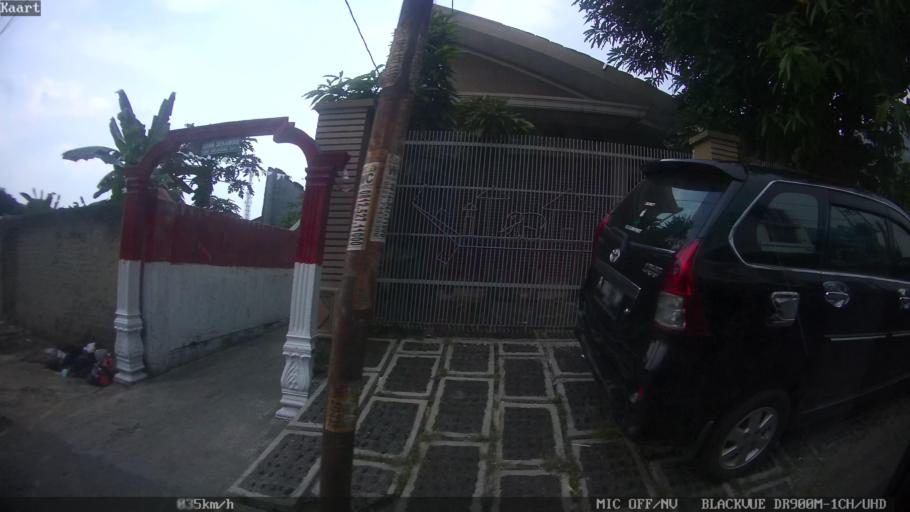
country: ID
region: Lampung
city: Bandarlampung
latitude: -5.4245
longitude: 105.2528
